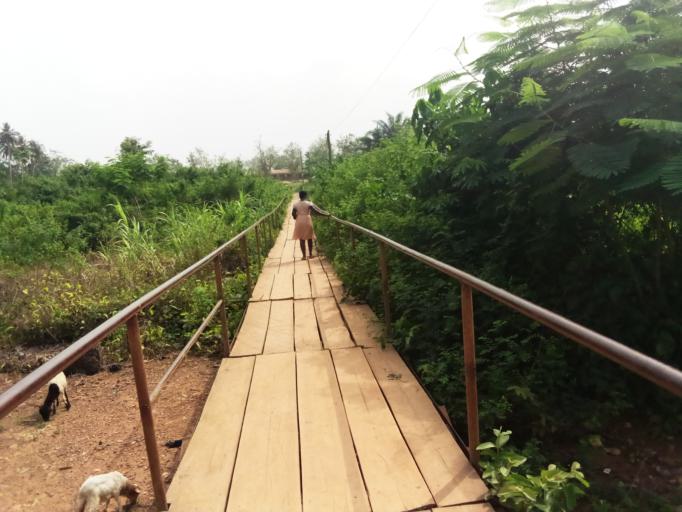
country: CI
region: Sud-Comoe
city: Ayame
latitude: 5.8258
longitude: -2.8192
